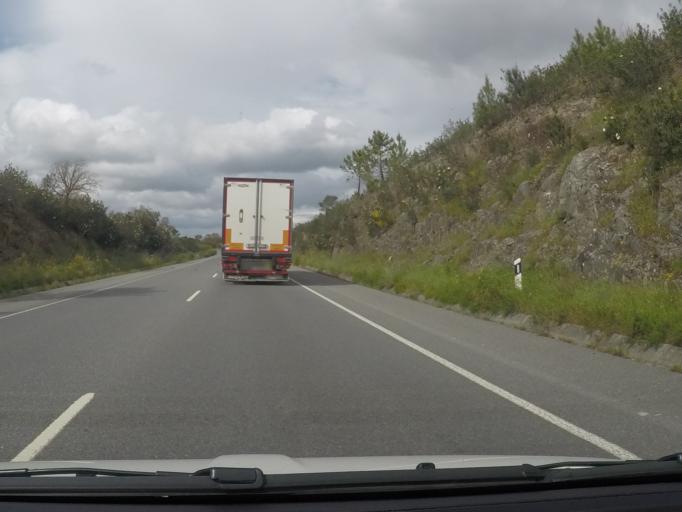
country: PT
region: Setubal
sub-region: Grandola
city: Grandola
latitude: 38.1435
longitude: -8.6511
